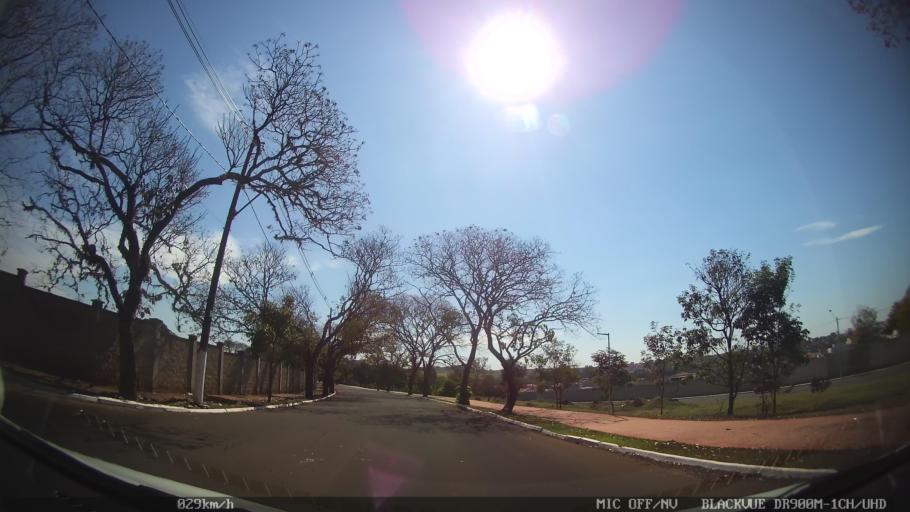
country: BR
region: Sao Paulo
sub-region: Santa Barbara D'Oeste
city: Santa Barbara d'Oeste
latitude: -22.7401
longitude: -47.4132
